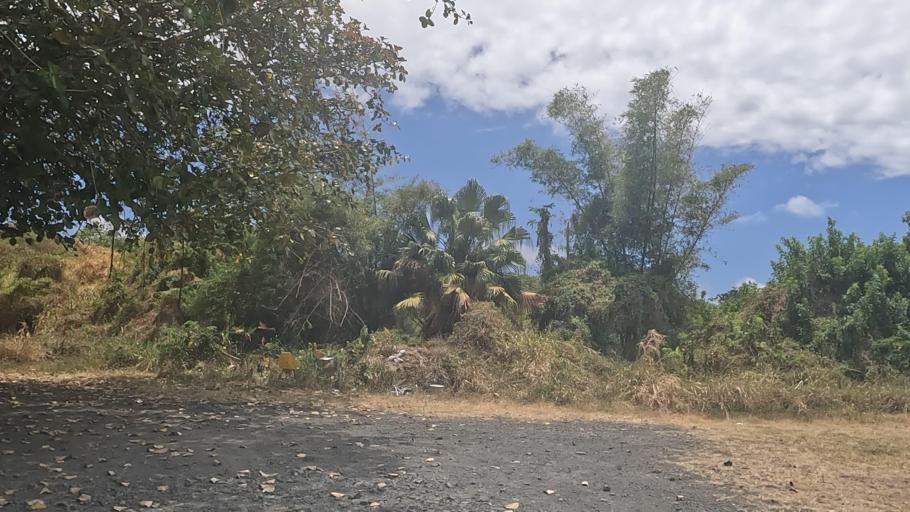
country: RE
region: Reunion
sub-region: Reunion
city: Saint-Benoit
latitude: -21.0341
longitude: 55.7179
